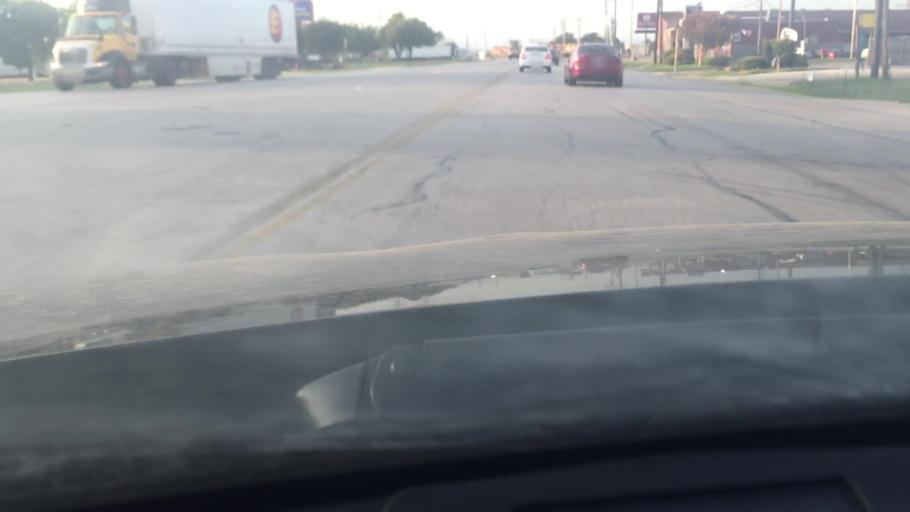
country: US
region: Texas
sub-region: Tarrant County
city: Blue Mound
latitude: 32.8410
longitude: -97.3431
